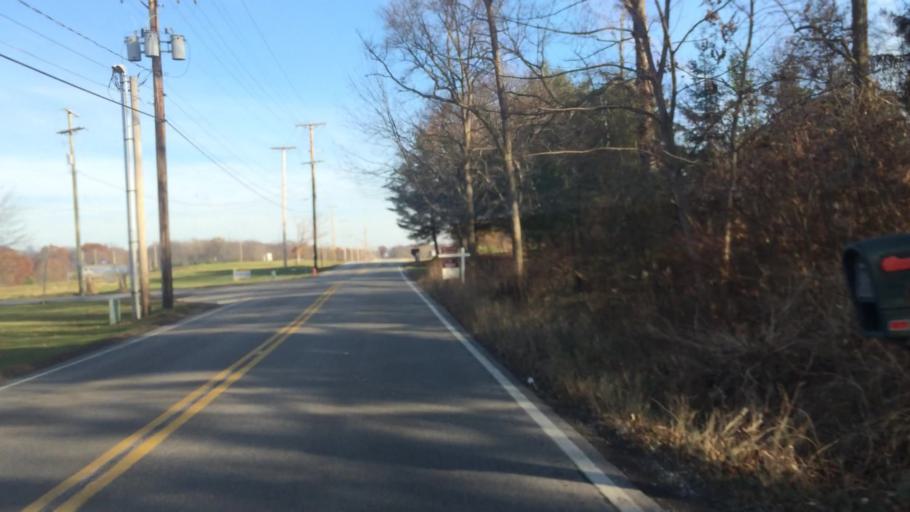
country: US
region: Ohio
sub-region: Summit County
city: Hudson
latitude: 41.2030
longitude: -81.4671
